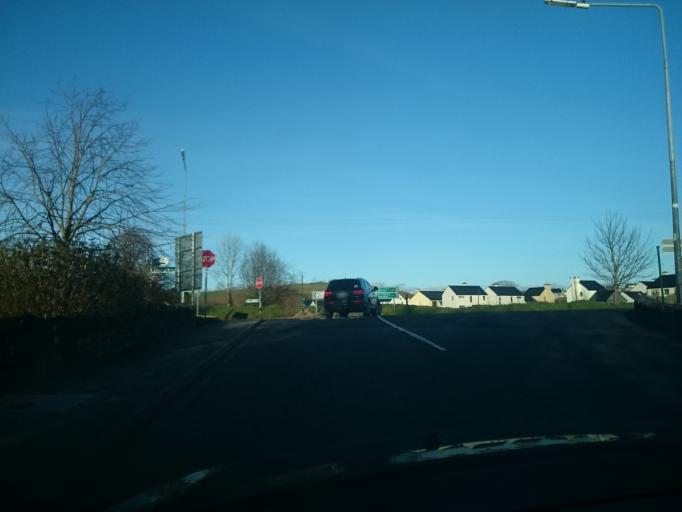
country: IE
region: Connaught
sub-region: Maigh Eo
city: Westport
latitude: 53.8071
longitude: -9.5276
